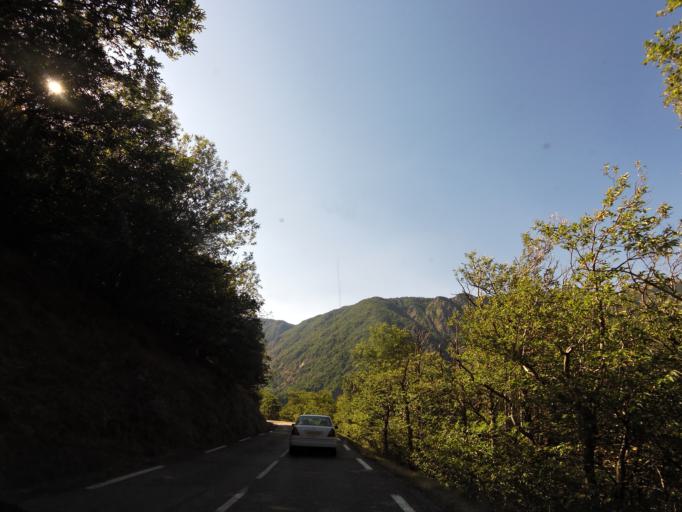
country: FR
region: Languedoc-Roussillon
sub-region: Departement du Gard
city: Valleraugue
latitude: 44.0919
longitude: 3.5779
